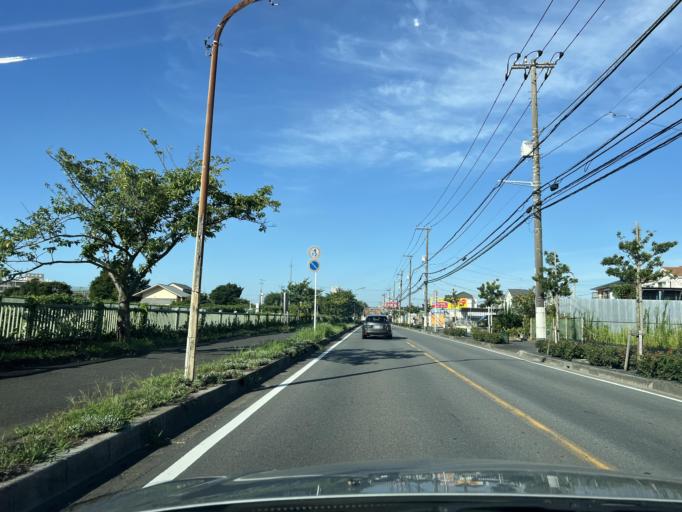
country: JP
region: Chiba
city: Funabashi
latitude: 35.7360
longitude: 139.9491
